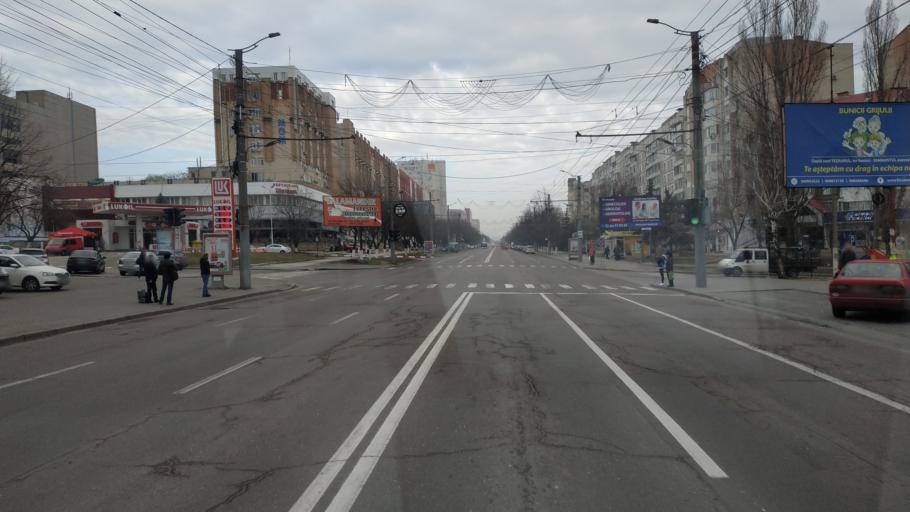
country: MD
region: Chisinau
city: Vatra
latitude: 47.0352
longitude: 28.7764
